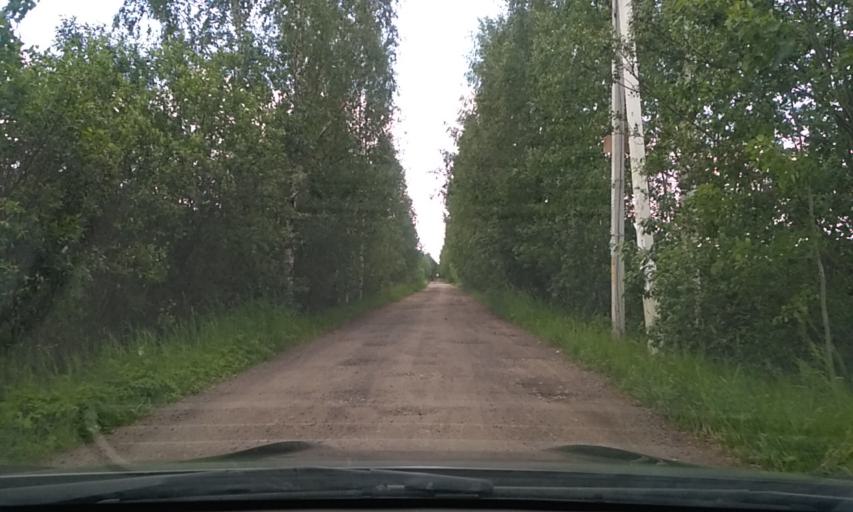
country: RU
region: Leningrad
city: Otradnoye
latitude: 59.8137
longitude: 30.8259
